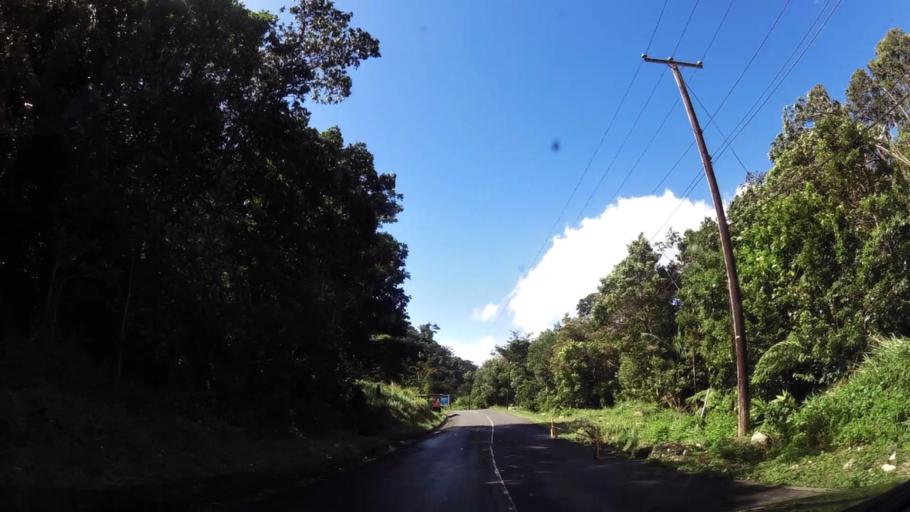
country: DM
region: Saint Paul
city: Pont Casse
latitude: 15.3740
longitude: -61.3452
